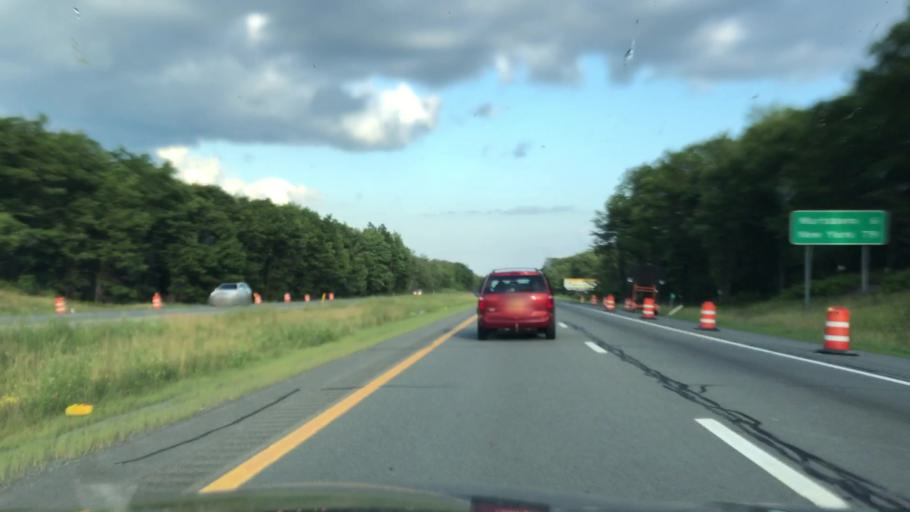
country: US
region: New York
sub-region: Sullivan County
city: Rock Hill
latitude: 41.6016
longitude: -74.5538
